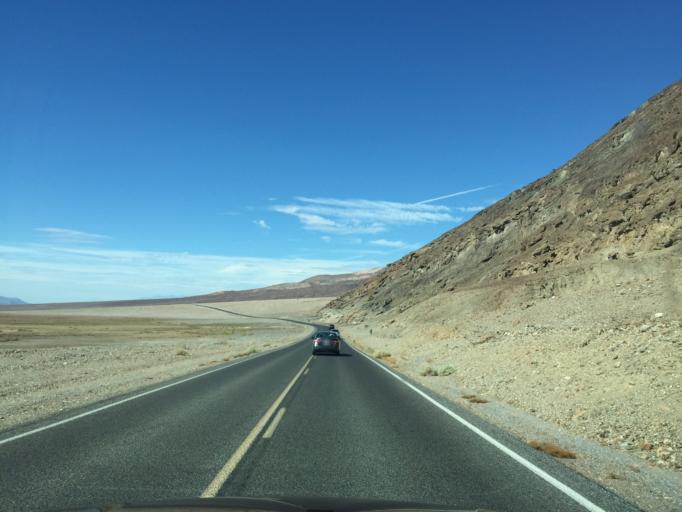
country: US
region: Nevada
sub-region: Nye County
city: Beatty
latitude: 36.2498
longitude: -116.7734
